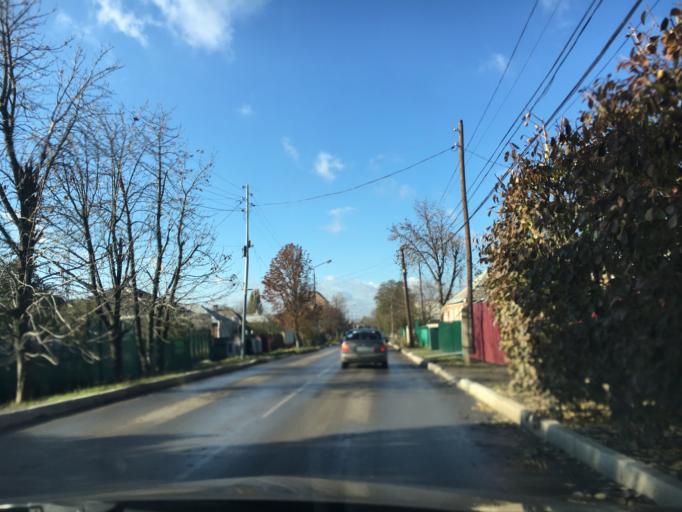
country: RU
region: Rostov
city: Matveyev Kurgan
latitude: 47.5662
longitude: 38.8696
